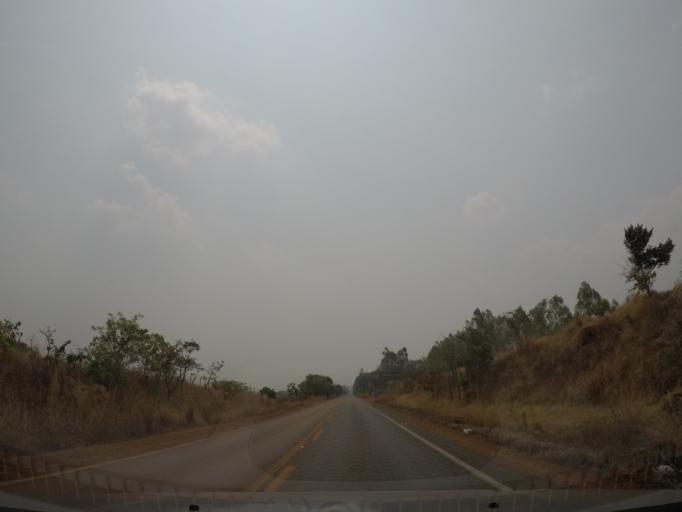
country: BR
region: Goias
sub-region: Pirenopolis
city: Pirenopolis
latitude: -15.9172
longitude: -48.8571
